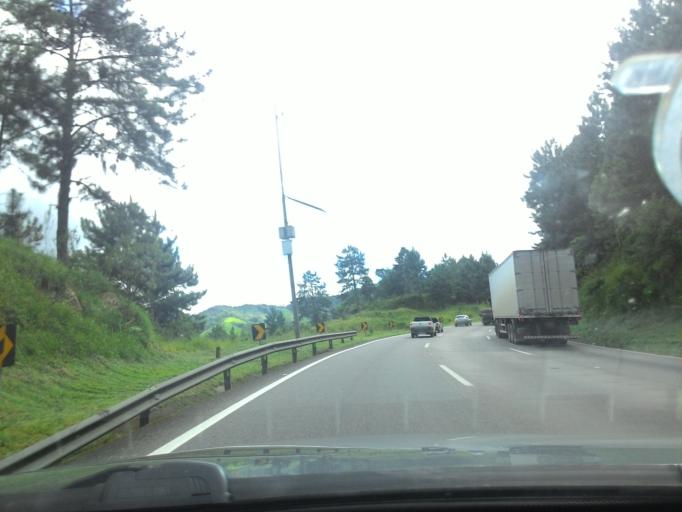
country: BR
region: Sao Paulo
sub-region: Cajati
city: Cajati
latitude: -24.8851
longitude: -48.2262
